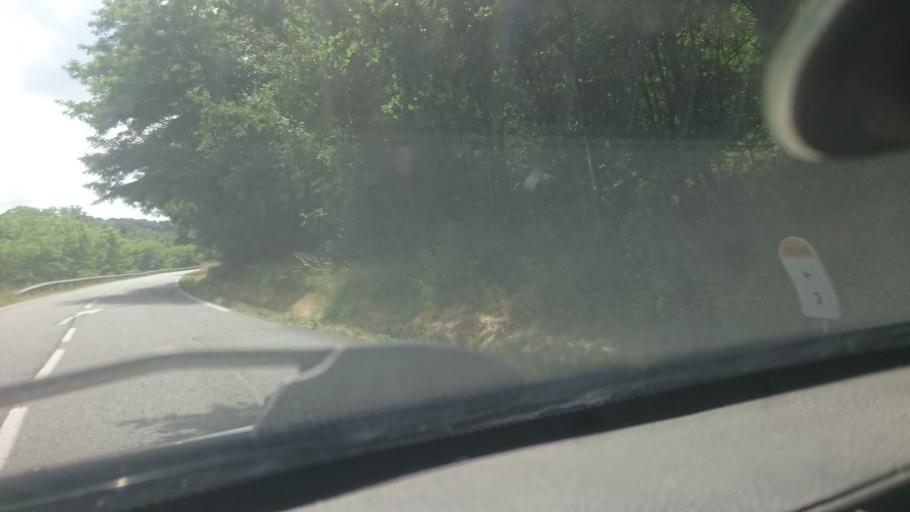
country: FR
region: Rhone-Alpes
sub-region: Departement du Rhone
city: Lentilly
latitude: 45.8525
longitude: 4.6492
